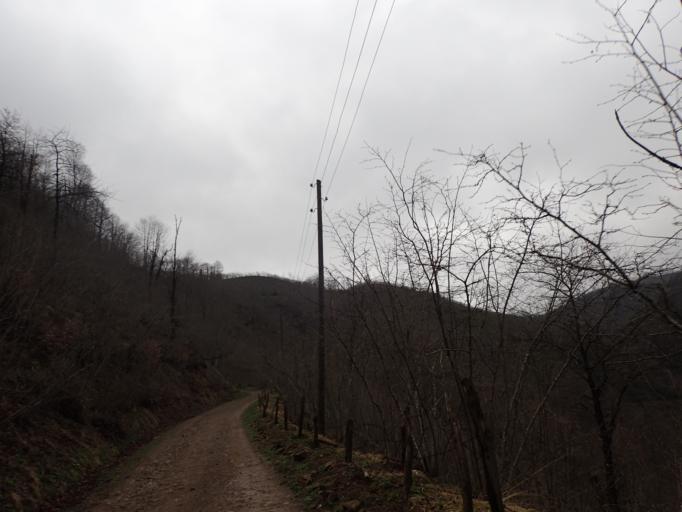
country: TR
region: Ordu
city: Camas
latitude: 40.8678
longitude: 37.5079
